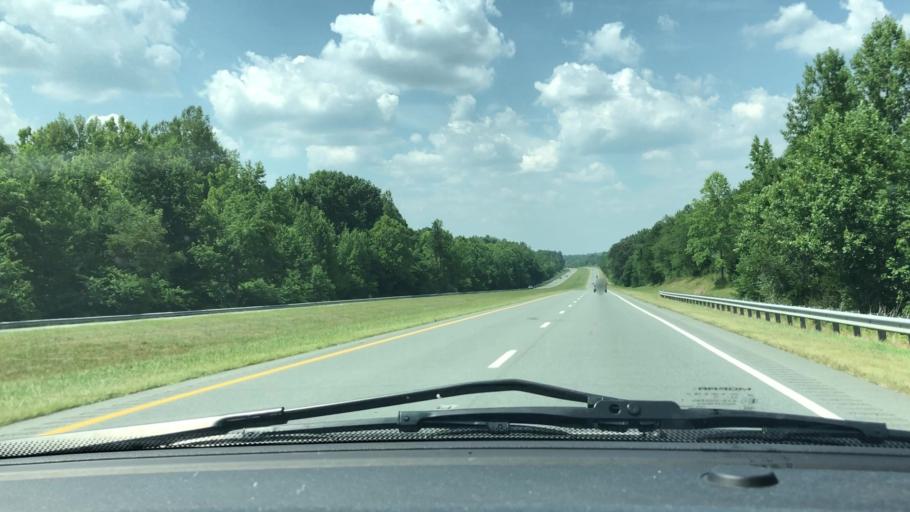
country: US
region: North Carolina
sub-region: Guilford County
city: Forest Oaks
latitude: 35.9397
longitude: -79.6859
